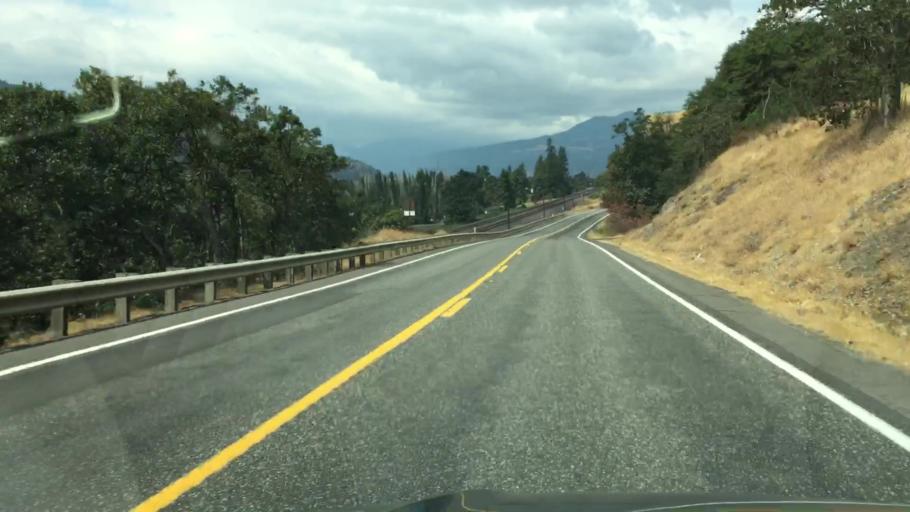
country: US
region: Washington
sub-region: Klickitat County
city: White Salmon
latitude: 45.7038
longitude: -121.4366
